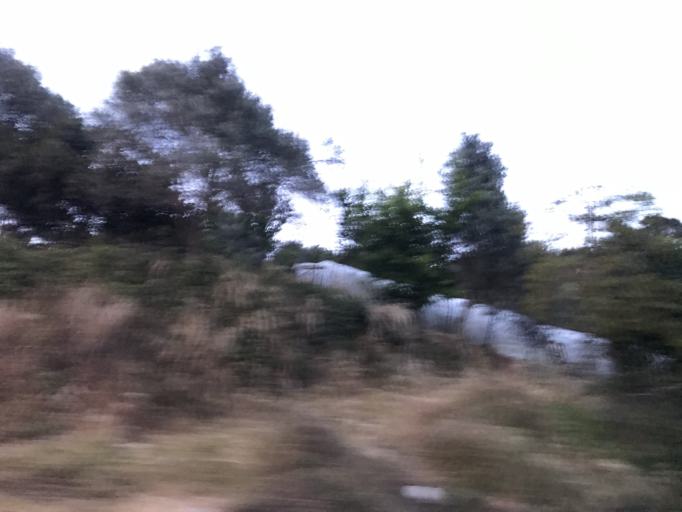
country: TR
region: Hatay
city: Uzunbag
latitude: 36.1322
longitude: 36.0415
